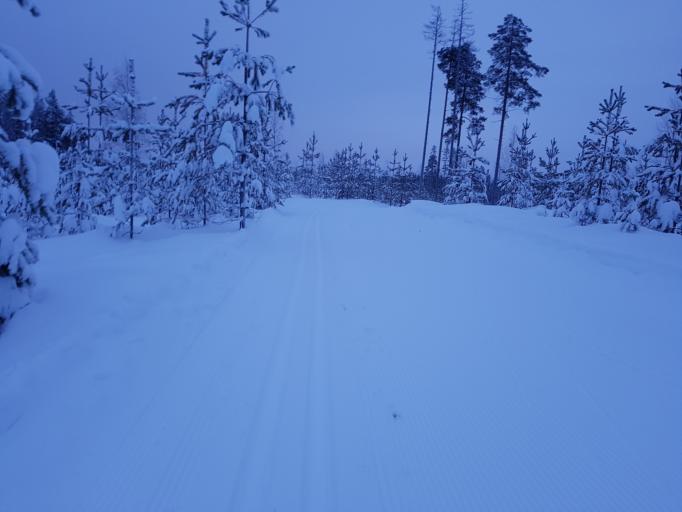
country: FI
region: Kainuu
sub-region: Kehys-Kainuu
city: Kuhmo
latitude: 64.0871
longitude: 29.5164
